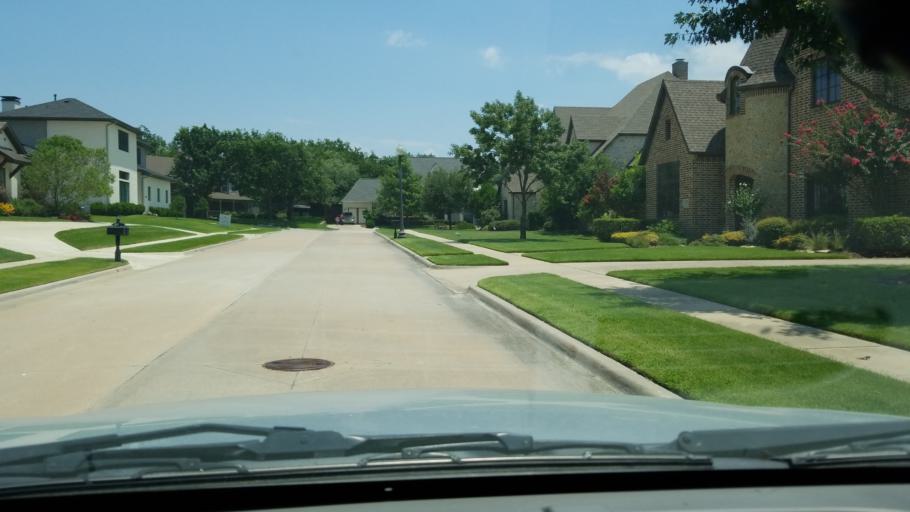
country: US
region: Texas
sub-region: Dallas County
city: Coppell
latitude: 32.9578
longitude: -96.9906
